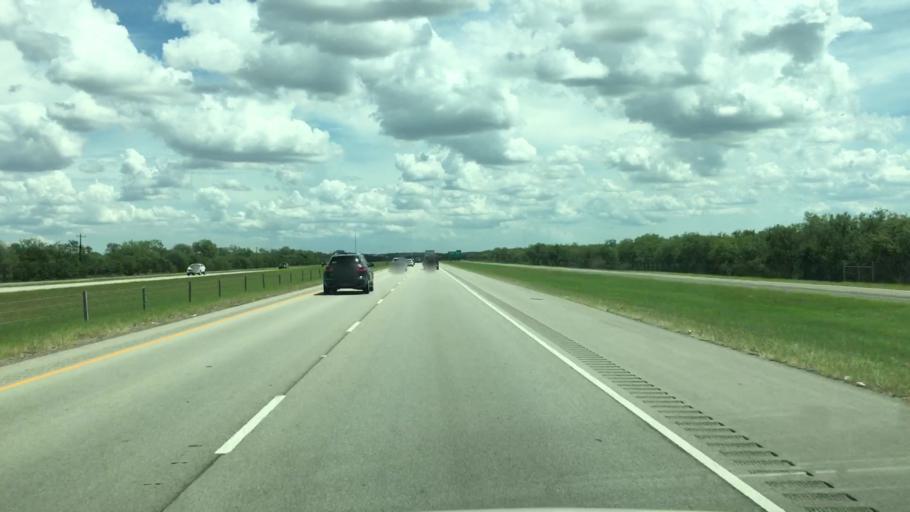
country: US
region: Texas
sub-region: Live Oak County
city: George West
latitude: 28.2776
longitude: -97.9523
